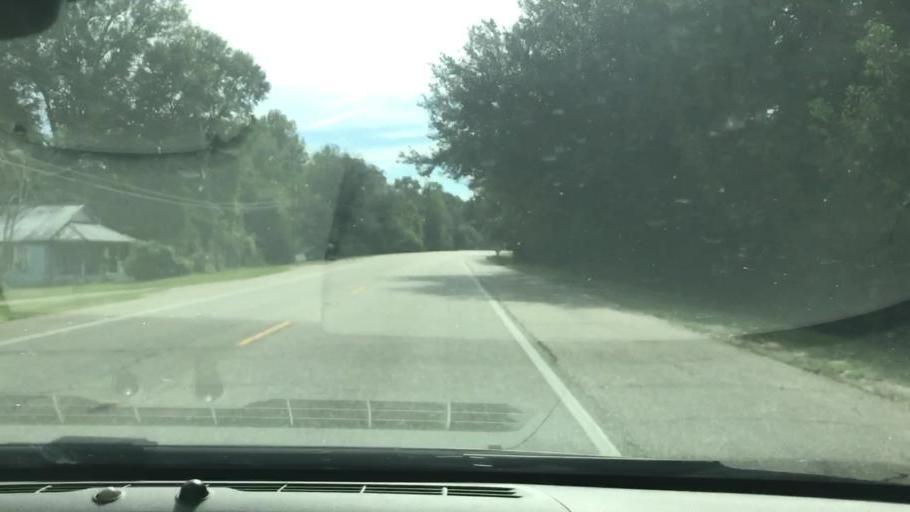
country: US
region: Mississippi
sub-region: Pearl River County
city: Nicholson
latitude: 30.4918
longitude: -89.8113
